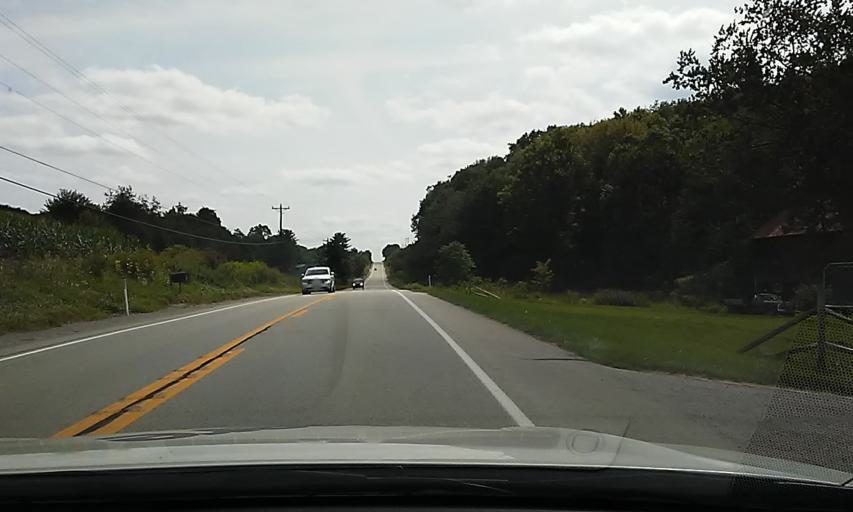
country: US
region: Pennsylvania
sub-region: Indiana County
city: Clymer
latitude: 40.8035
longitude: -79.0552
